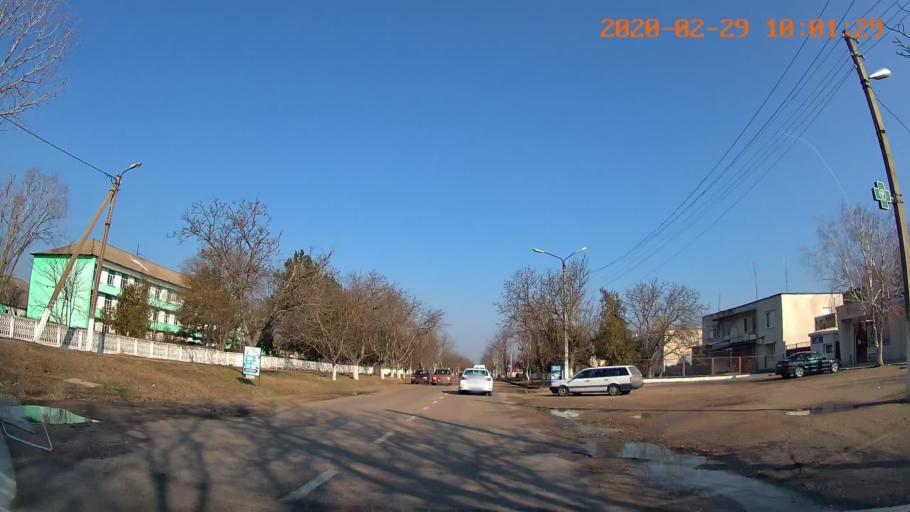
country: MD
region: Telenesti
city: Slobozia
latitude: 46.7757
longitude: 29.6846
